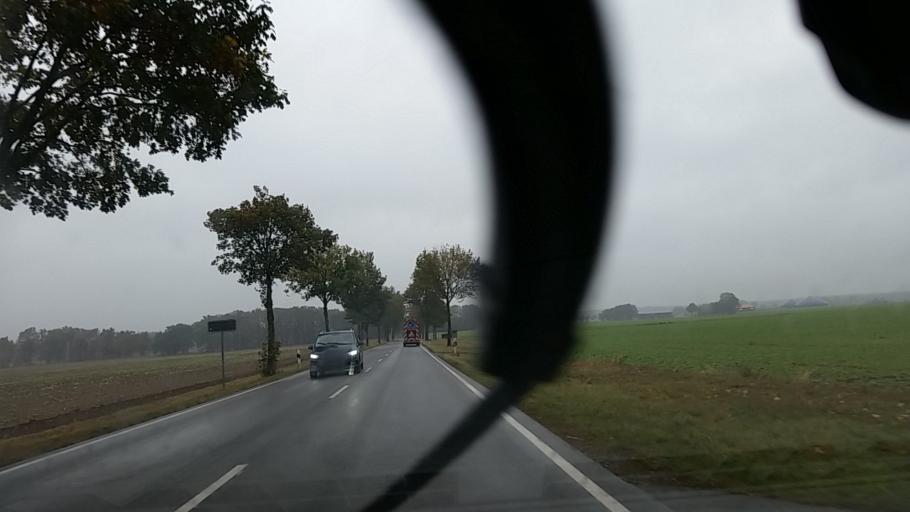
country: DE
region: Lower Saxony
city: Luder
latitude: 52.7885
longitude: 10.7156
